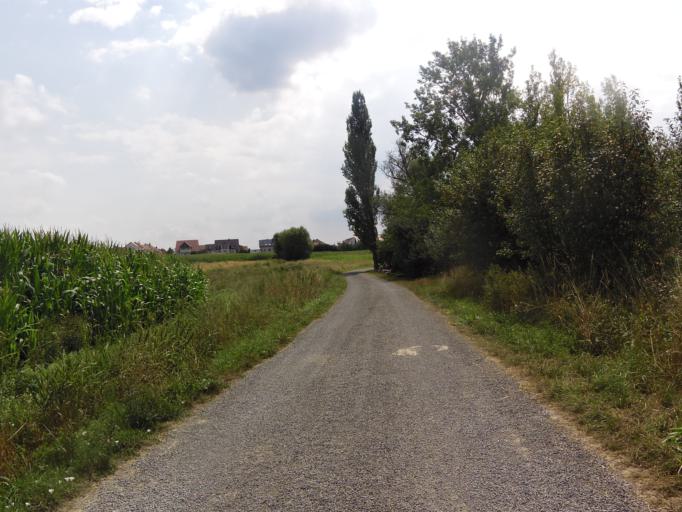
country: DE
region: Bavaria
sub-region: Regierungsbezirk Unterfranken
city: Eibelstadt
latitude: 49.7291
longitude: 9.9694
